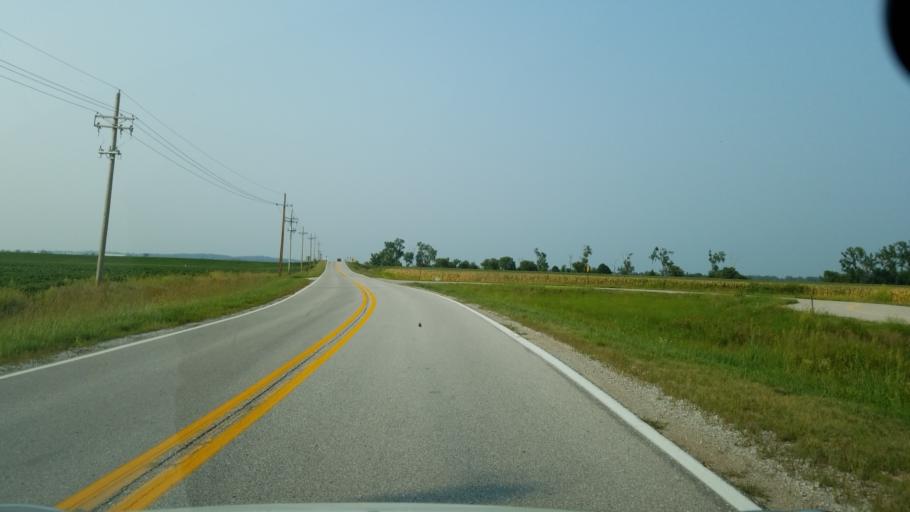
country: US
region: Nebraska
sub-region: Sarpy County
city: Offutt Air Force Base
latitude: 41.0785
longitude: -95.8898
